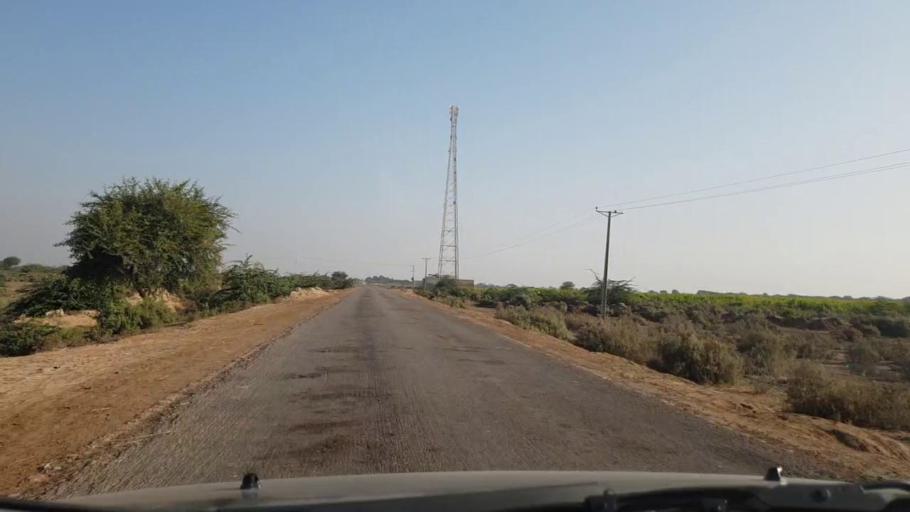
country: PK
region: Sindh
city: Tando Bago
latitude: 24.8546
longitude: 69.0405
